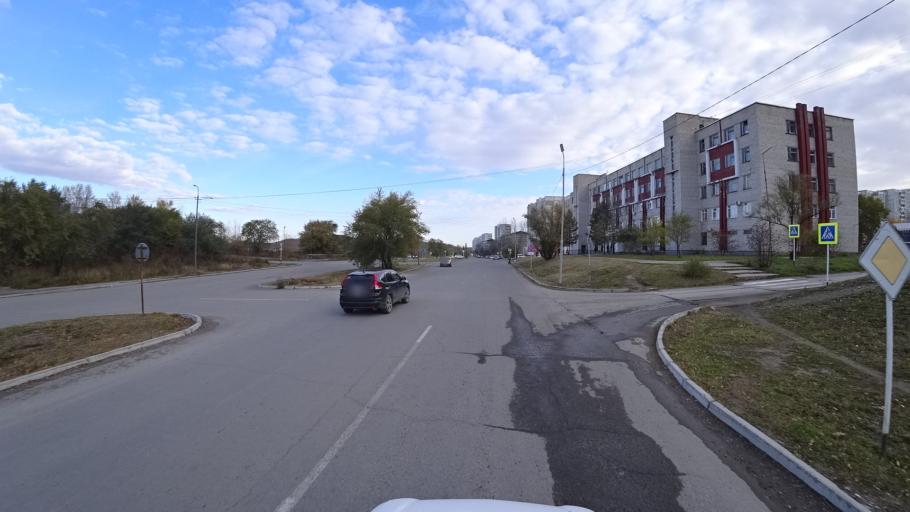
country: RU
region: Khabarovsk Krai
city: Amursk
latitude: 50.2424
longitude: 136.9142
